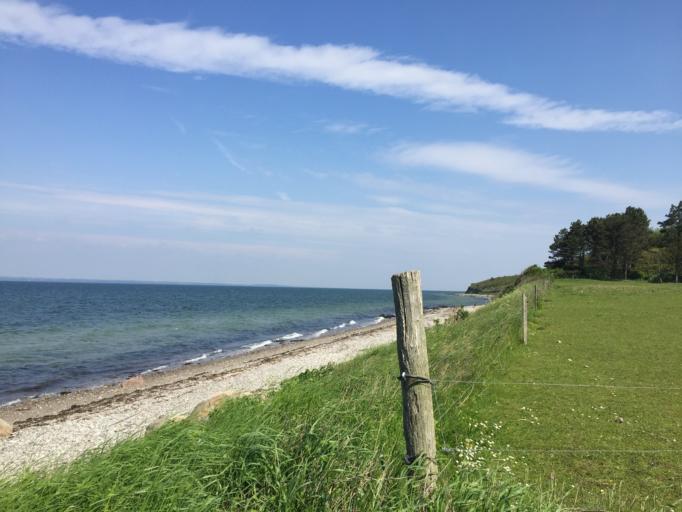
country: DK
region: South Denmark
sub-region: Langeland Kommune
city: Rudkobing
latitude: 55.0148
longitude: 10.8260
